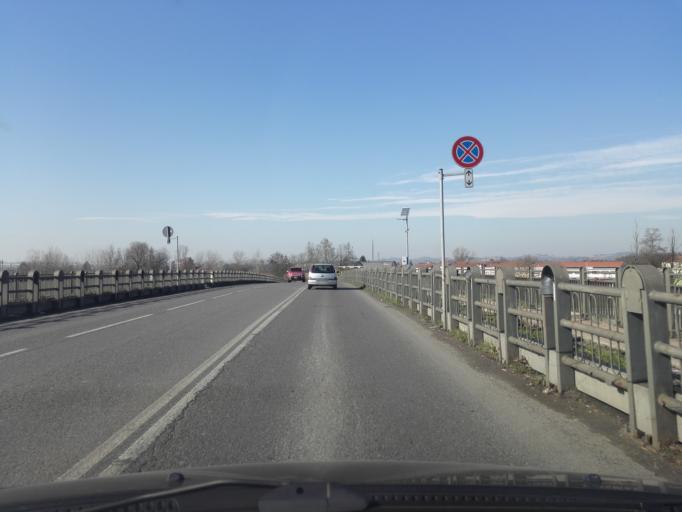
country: IT
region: Piedmont
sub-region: Provincia di Alessandria
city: Alessandria
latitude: 44.9142
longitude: 8.6026
